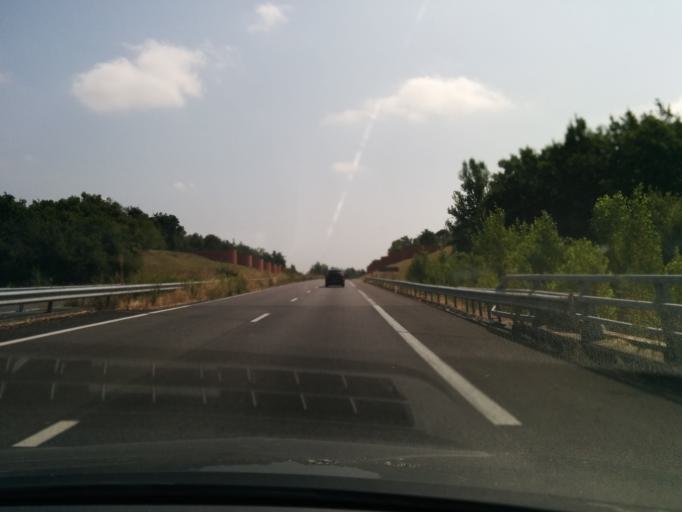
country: FR
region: Midi-Pyrenees
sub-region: Departement de la Haute-Garonne
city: Montastruc-la-Conseillere
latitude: 43.7459
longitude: 1.6099
